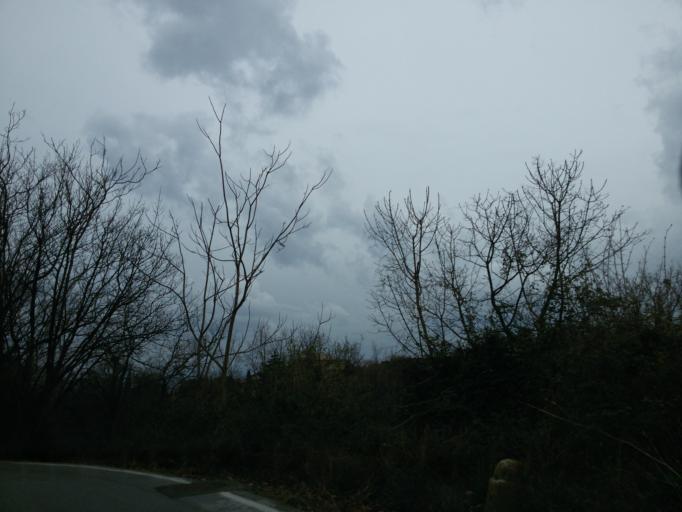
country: IT
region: Liguria
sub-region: Provincia di Genova
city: Genoa
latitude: 44.4176
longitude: 8.9758
